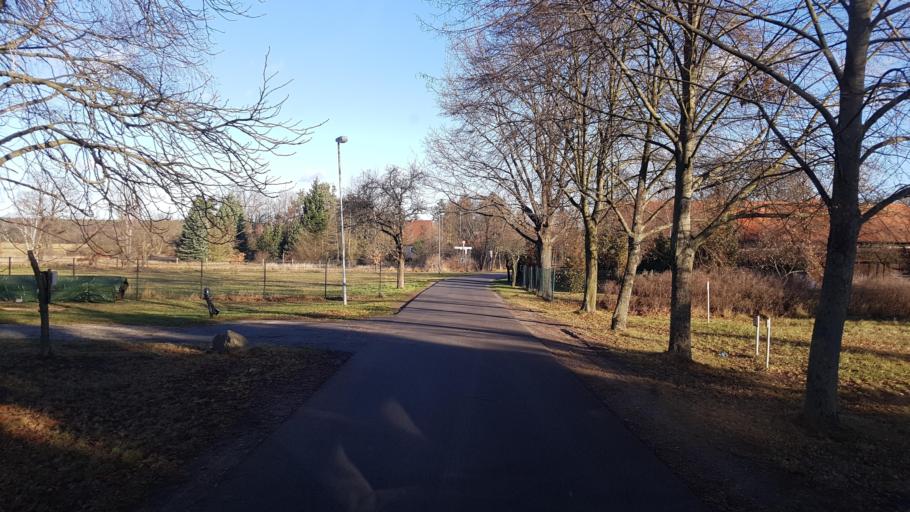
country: DE
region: Brandenburg
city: Heinersbruck
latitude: 51.7468
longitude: 14.5422
